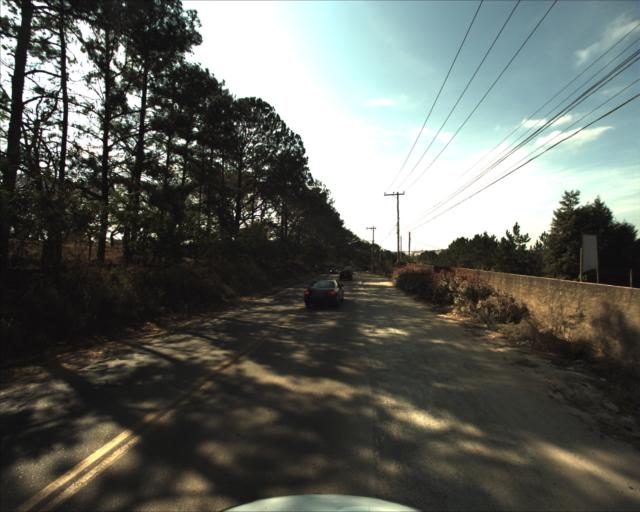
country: BR
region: Sao Paulo
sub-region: Sorocaba
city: Sorocaba
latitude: -23.4424
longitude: -47.5257
